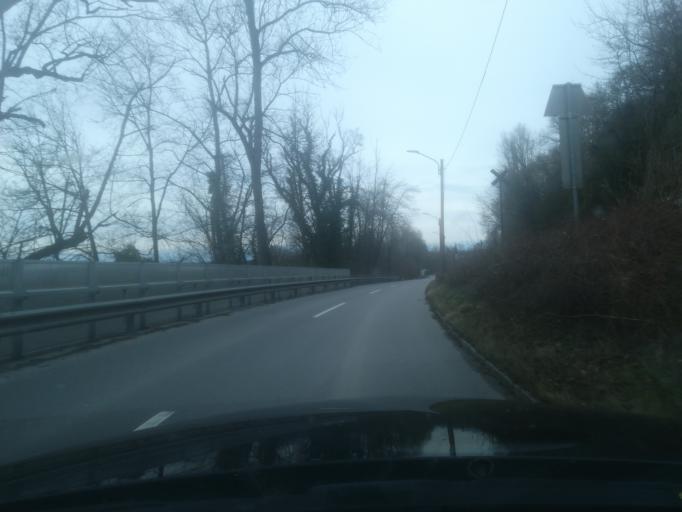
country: AT
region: Upper Austria
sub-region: Wels-Land
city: Steinhaus
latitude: 48.1366
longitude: 14.0083
